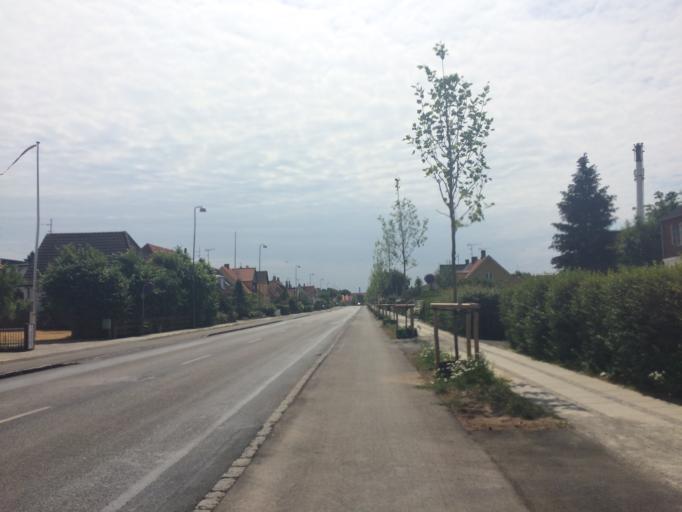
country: DK
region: Capital Region
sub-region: Bornholm Kommune
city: Ronne
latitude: 55.1142
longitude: 14.7051
